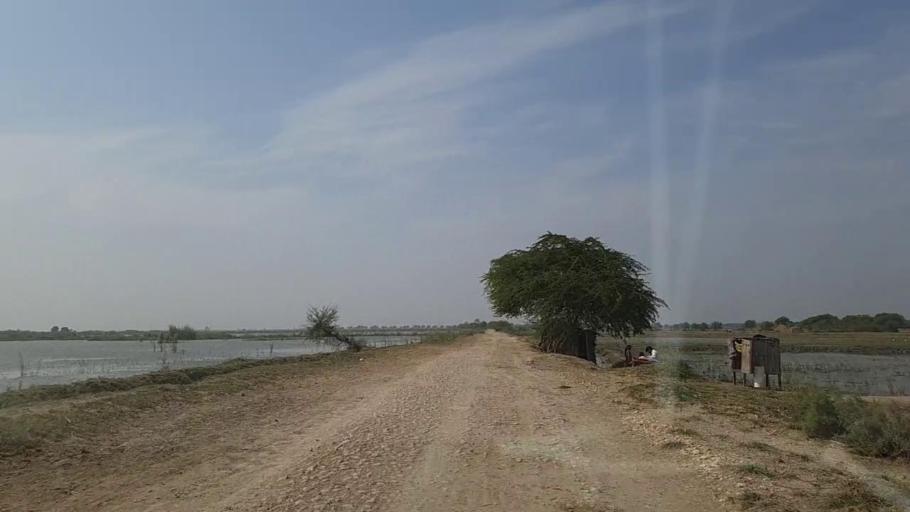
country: PK
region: Sindh
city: Mirpur Batoro
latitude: 24.6103
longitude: 68.2201
